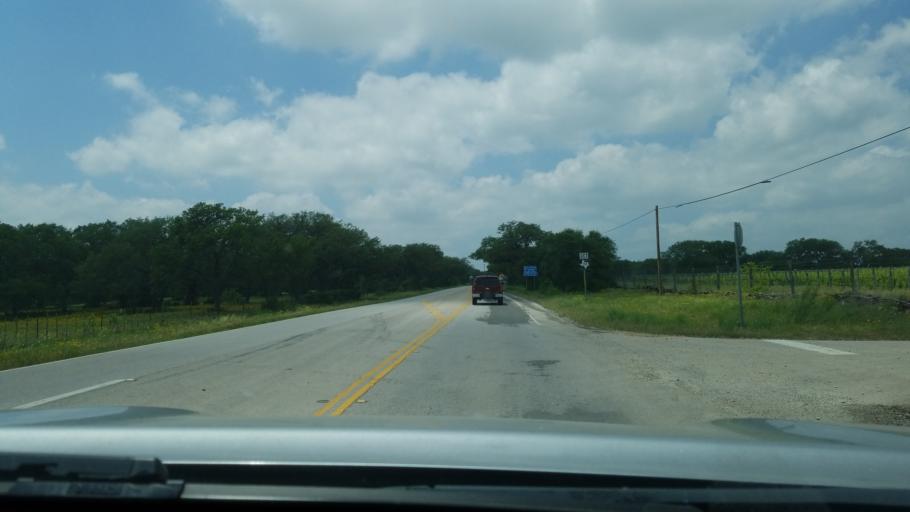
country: US
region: Texas
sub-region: Hays County
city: Dripping Springs
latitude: 30.1317
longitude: -98.0267
